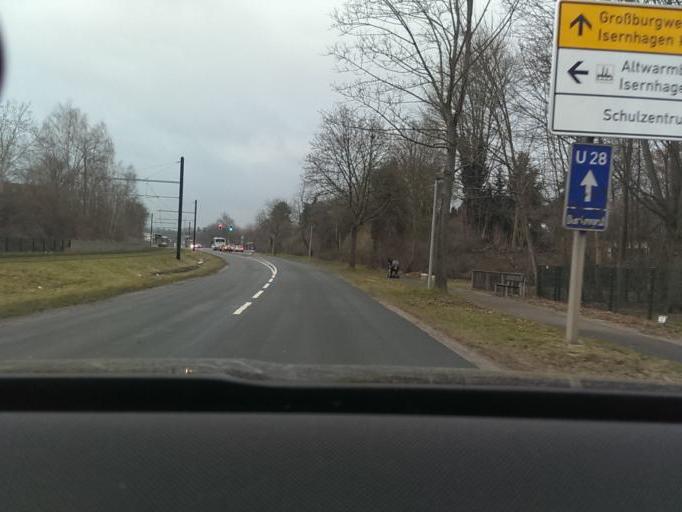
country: DE
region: Lower Saxony
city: Isernhagen Farster Bauerschaft
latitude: 52.4352
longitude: 9.8476
